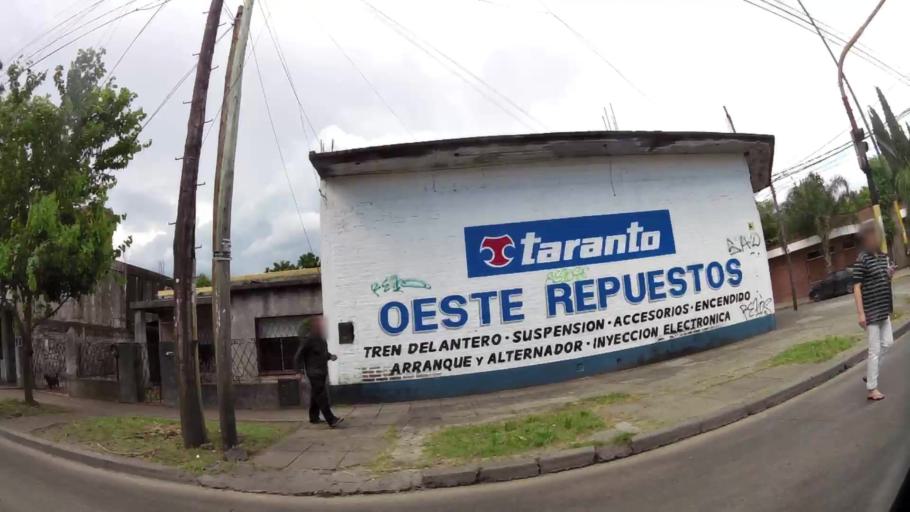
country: AR
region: Buenos Aires
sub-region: Partido de Merlo
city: Merlo
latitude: -34.6327
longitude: -58.6988
